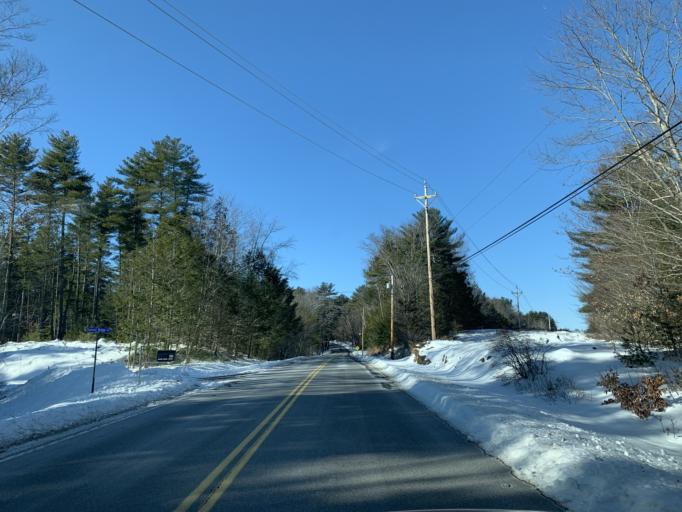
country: US
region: Maine
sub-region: York County
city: Ogunquit
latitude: 43.2480
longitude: -70.6186
